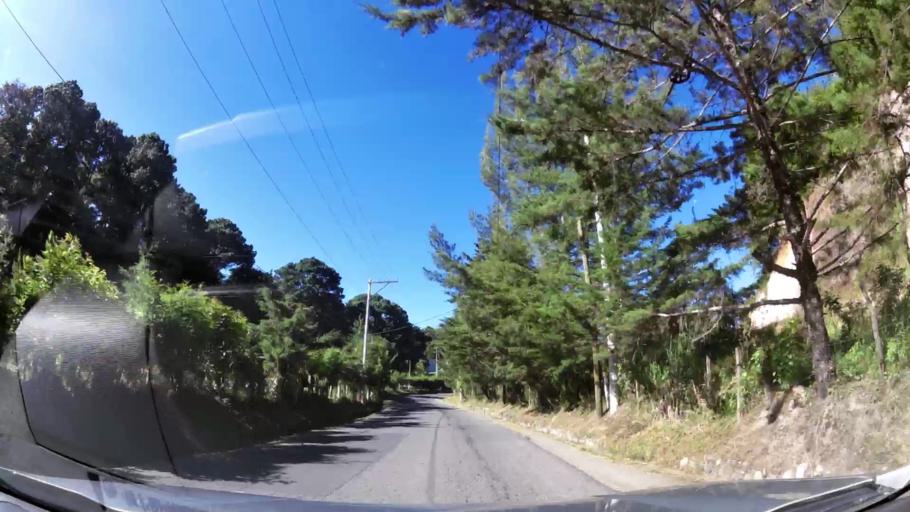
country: GT
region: Guatemala
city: Fraijanes
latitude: 14.4550
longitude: -90.4408
